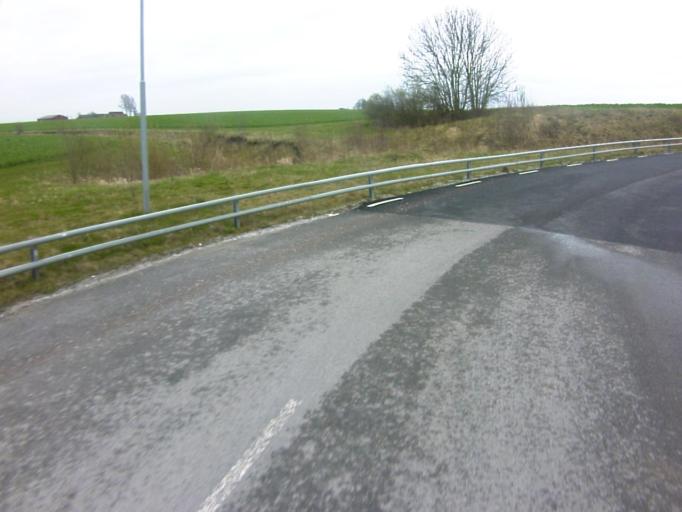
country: SE
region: Skane
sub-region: Kavlinge Kommun
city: Kaevlinge
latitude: 55.7694
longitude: 13.0881
